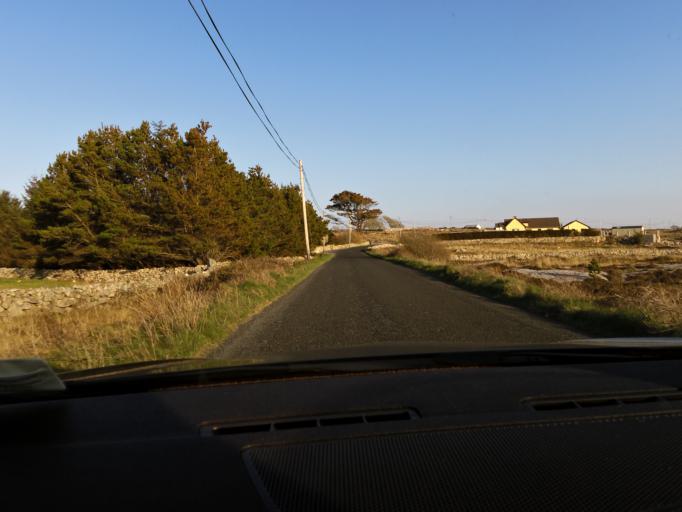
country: IE
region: Connaught
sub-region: County Galway
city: Oughterard
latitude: 53.2638
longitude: -9.5477
